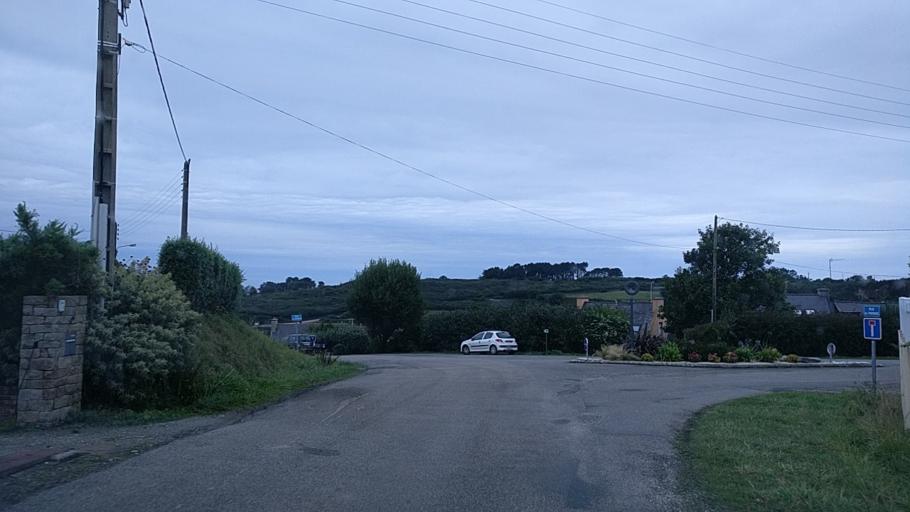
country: FR
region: Brittany
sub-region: Departement du Finistere
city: Saint-Pabu
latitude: 48.5714
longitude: -4.6058
